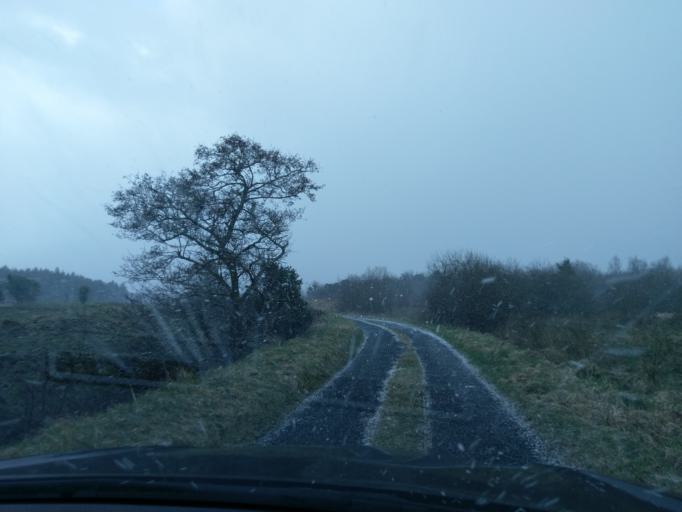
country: IE
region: Connaught
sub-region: County Galway
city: Athenry
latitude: 53.4052
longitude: -8.5935
